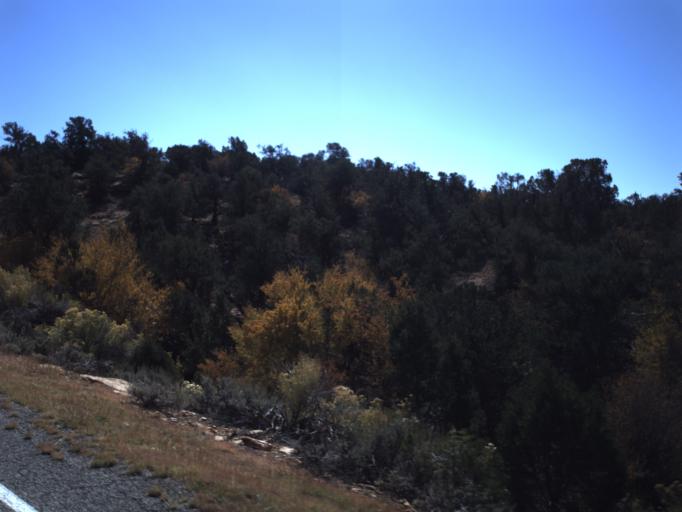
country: US
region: Utah
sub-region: San Juan County
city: Blanding
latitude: 37.5831
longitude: -109.8914
